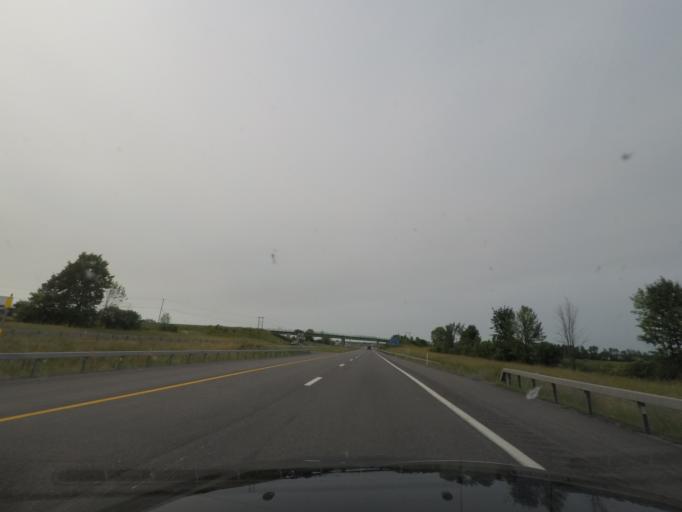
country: US
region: New York
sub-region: Clinton County
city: Champlain
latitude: 44.9713
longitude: -73.4517
